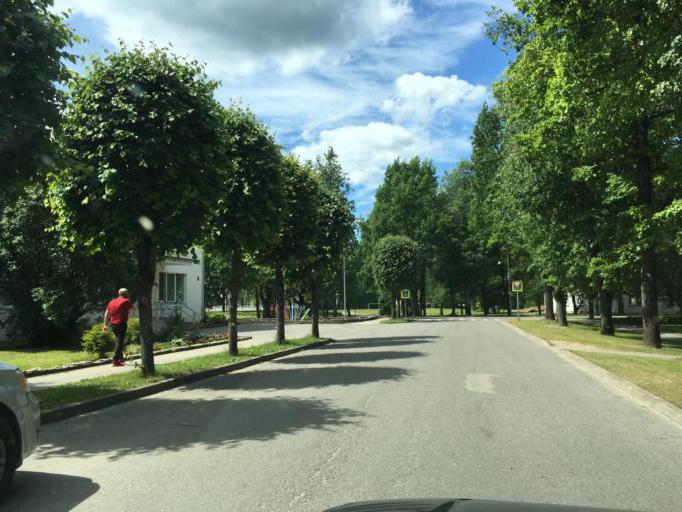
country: LV
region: Balvu Rajons
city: Balvi
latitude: 57.1306
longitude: 27.2647
